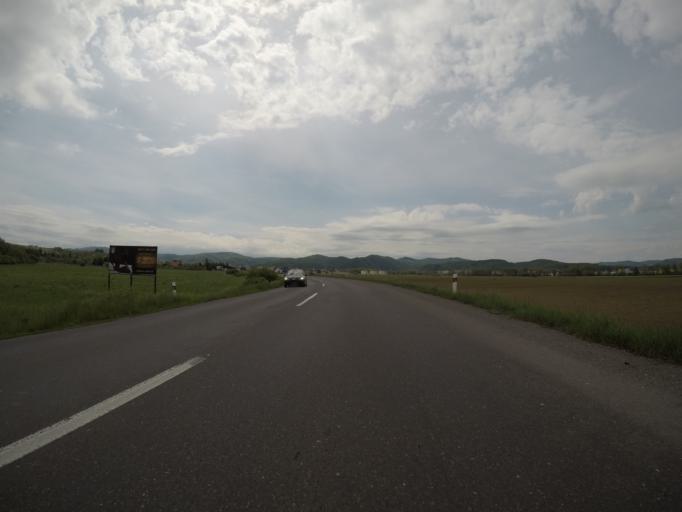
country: SK
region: Banskobystricky
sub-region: Okres Banska Bystrica
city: Zvolen
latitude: 48.5951
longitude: 19.1224
